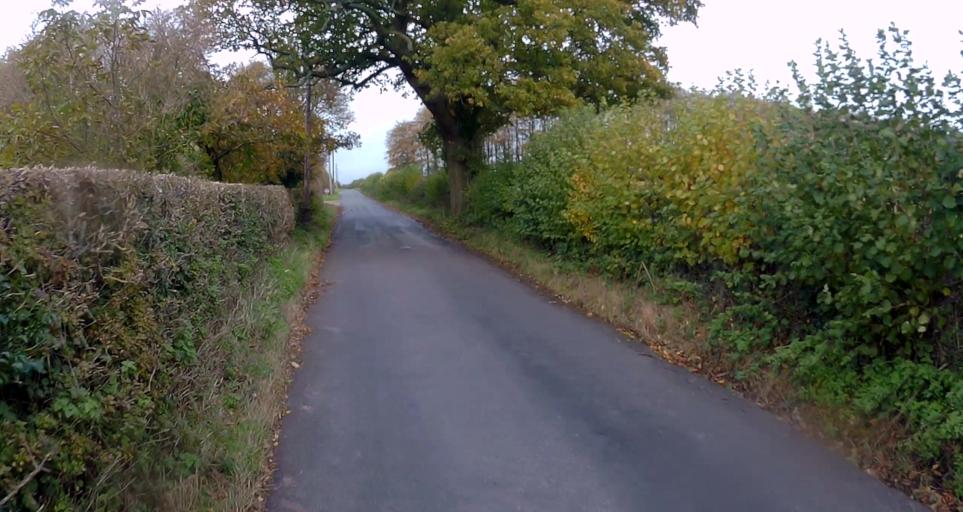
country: GB
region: England
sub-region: Hampshire
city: Four Marks
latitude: 51.1715
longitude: -1.0430
